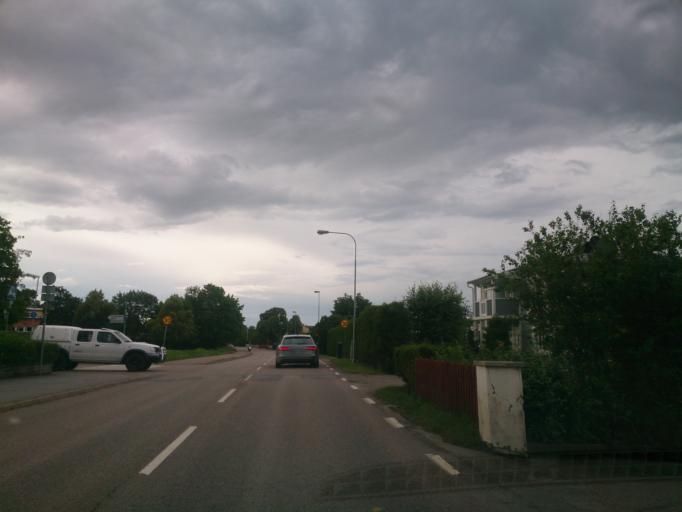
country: SE
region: OEstergoetland
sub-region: Linkopings Kommun
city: Malmslatt
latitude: 58.4155
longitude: 15.5195
